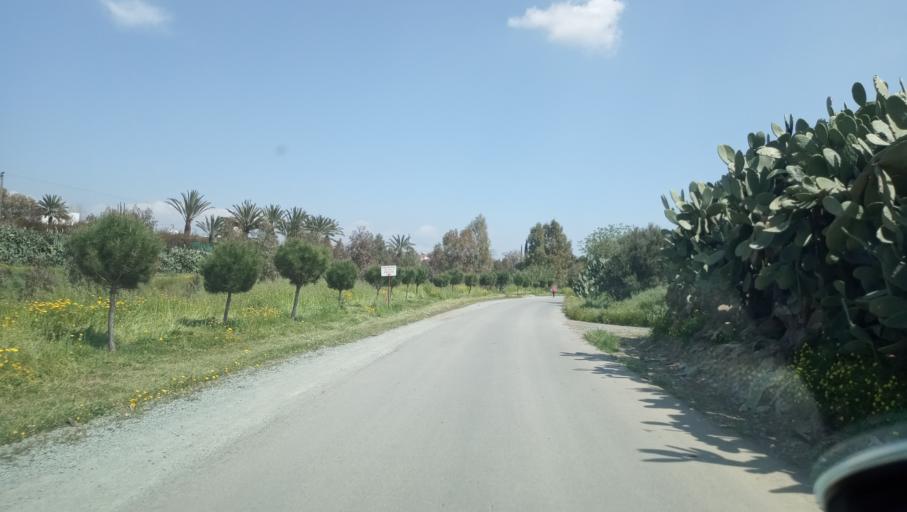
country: CY
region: Lefkosia
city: Dali
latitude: 35.0234
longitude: 33.4097
